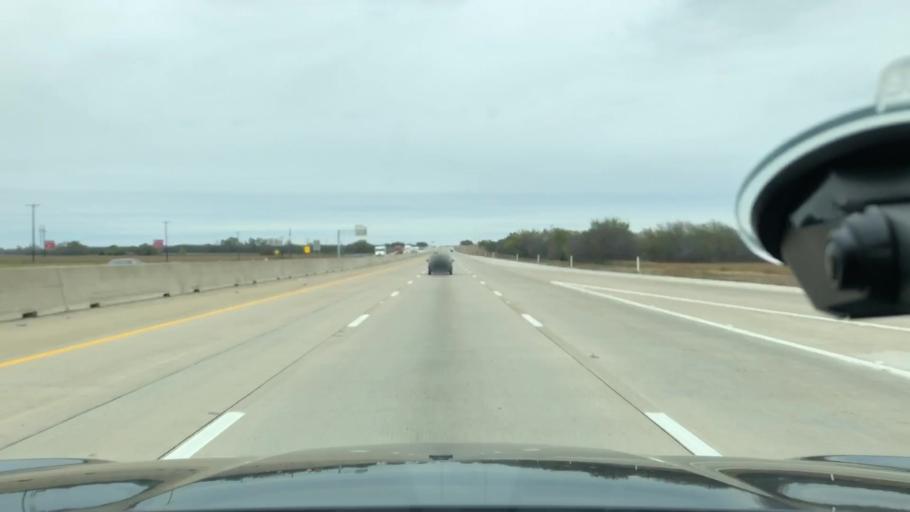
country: US
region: Texas
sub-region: Ellis County
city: Nash
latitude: 32.2632
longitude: -96.8721
